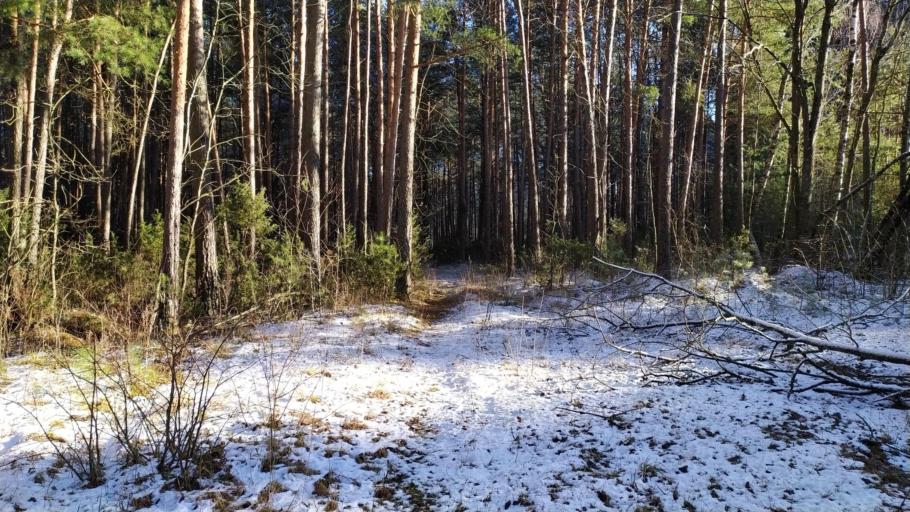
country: BY
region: Brest
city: Kamyanyets
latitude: 52.3770
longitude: 23.8696
